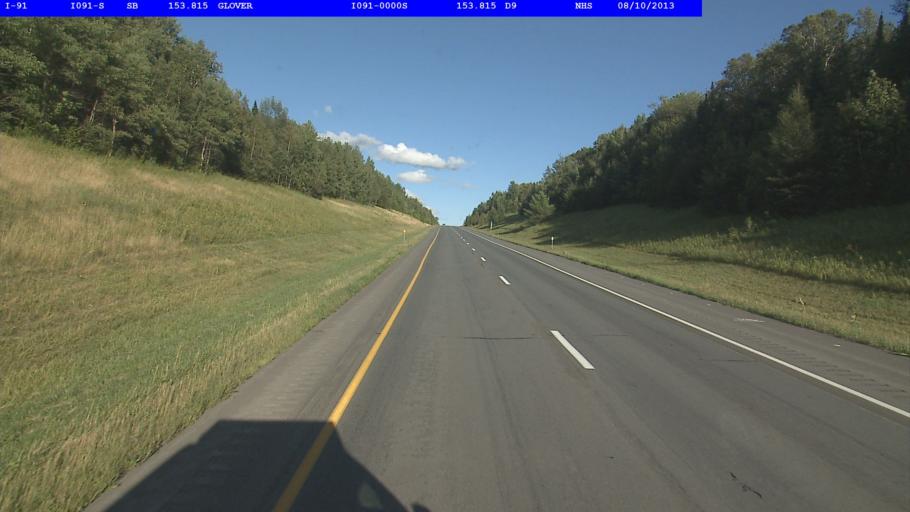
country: US
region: Vermont
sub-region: Orleans County
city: Newport
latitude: 44.7093
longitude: -72.1663
